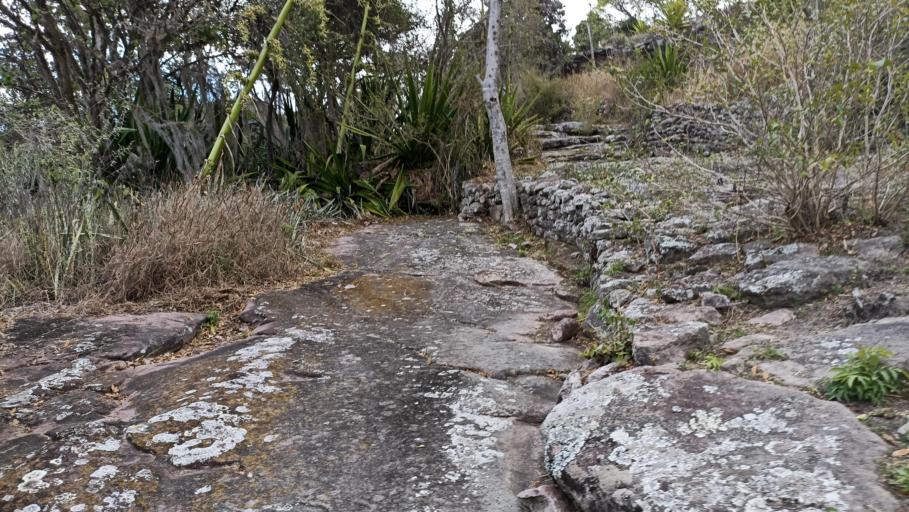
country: BR
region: Bahia
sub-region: Andarai
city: Vera Cruz
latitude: -12.8935
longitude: -41.3195
